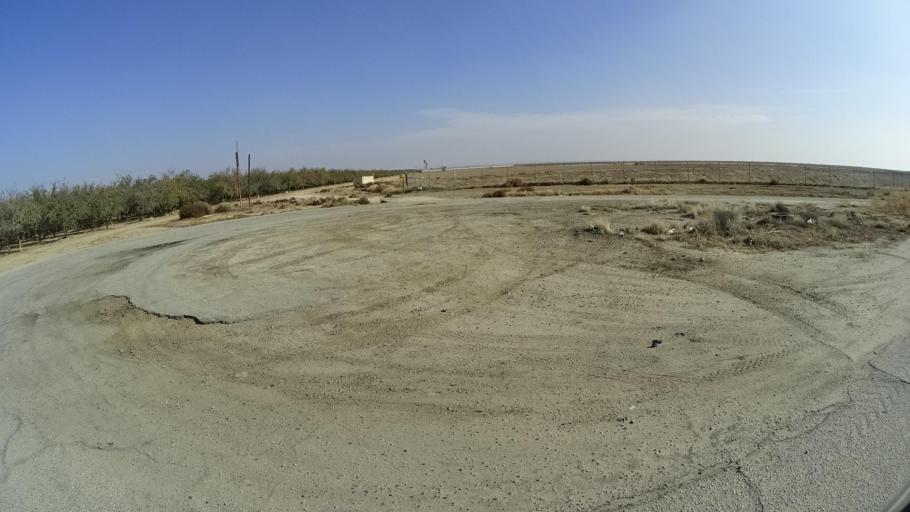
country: US
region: California
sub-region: Kern County
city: Shafter
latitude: 35.5367
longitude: -119.1868
